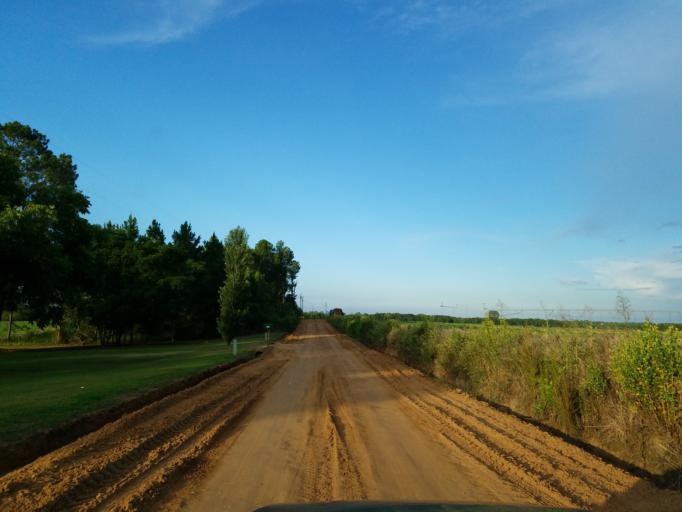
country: US
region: Georgia
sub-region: Turner County
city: Ashburn
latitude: 31.6416
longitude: -83.6104
